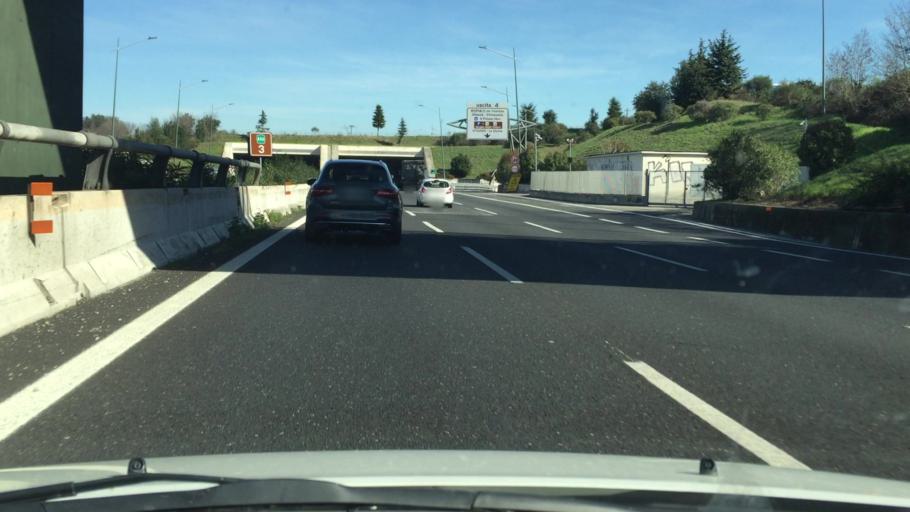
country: IT
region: Latium
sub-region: Citta metropolitana di Roma Capitale
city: Valle Santa
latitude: 41.9664
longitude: 12.4002
